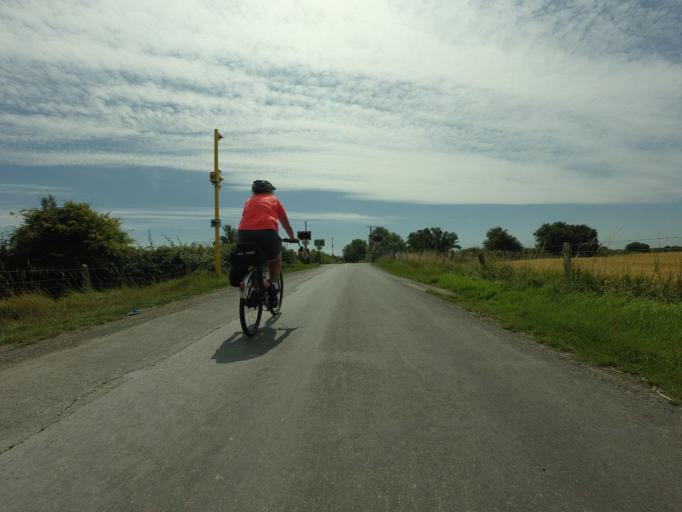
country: GB
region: England
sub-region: Kent
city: Stone
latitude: 51.0082
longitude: 0.7941
